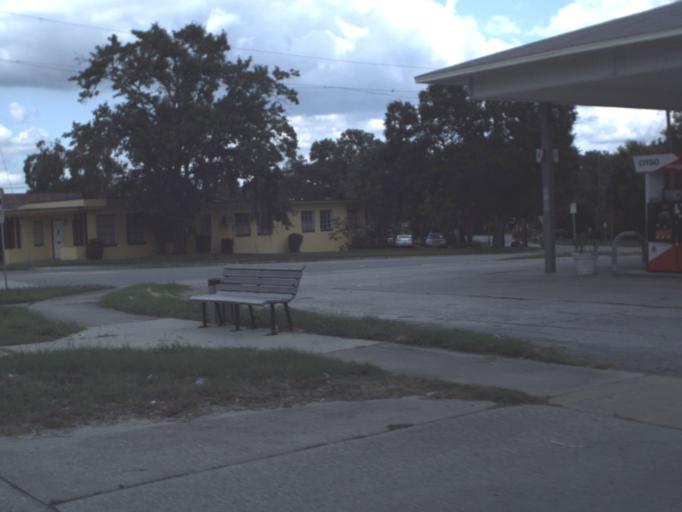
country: US
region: Florida
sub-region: Polk County
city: Lakeland
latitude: 28.0593
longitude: -81.9532
